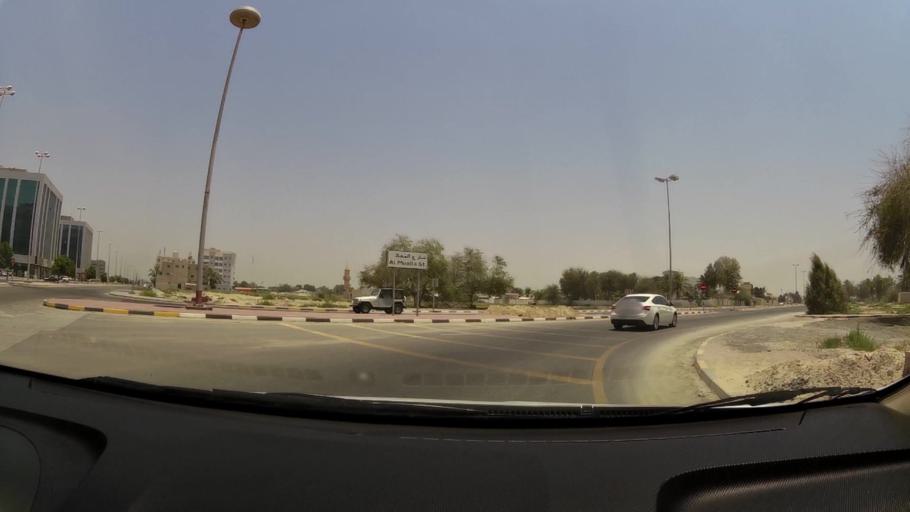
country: AE
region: Umm al Qaywayn
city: Umm al Qaywayn
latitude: 25.5773
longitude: 55.5558
